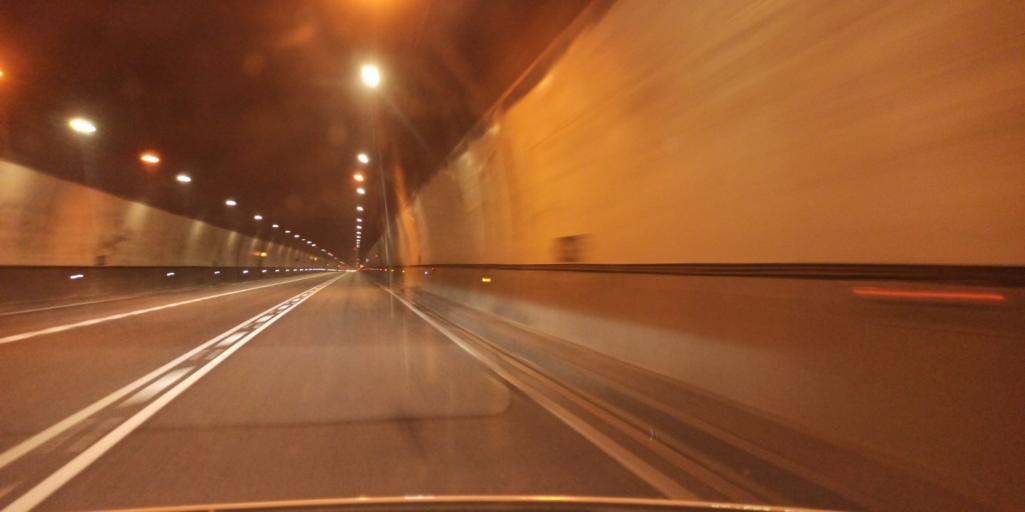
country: ES
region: Catalonia
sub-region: Provincia de Barcelona
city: Santa Maria de Corco
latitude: 42.0912
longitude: 2.3607
